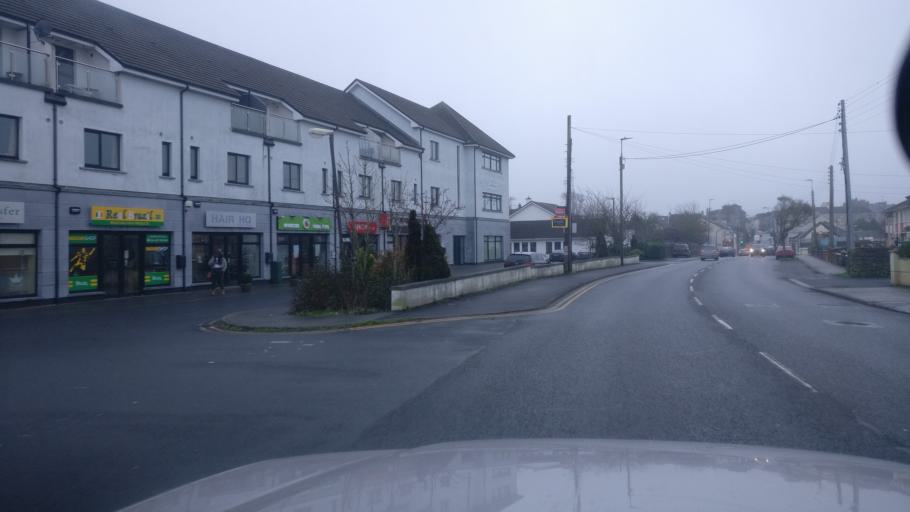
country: IE
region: Connaught
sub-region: County Galway
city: Gort
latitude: 53.0701
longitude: -8.8212
